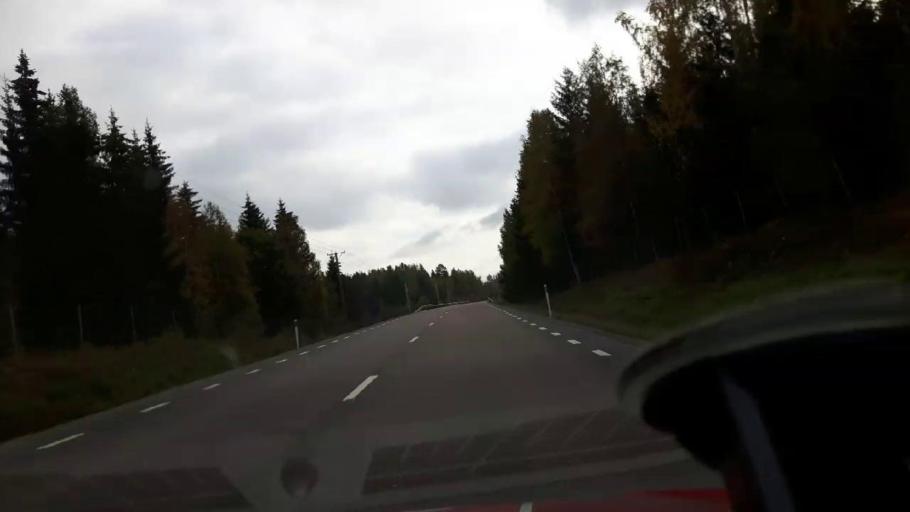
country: SE
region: Gaevleborg
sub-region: Bollnas Kommun
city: Kilafors
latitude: 61.2892
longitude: 16.5075
